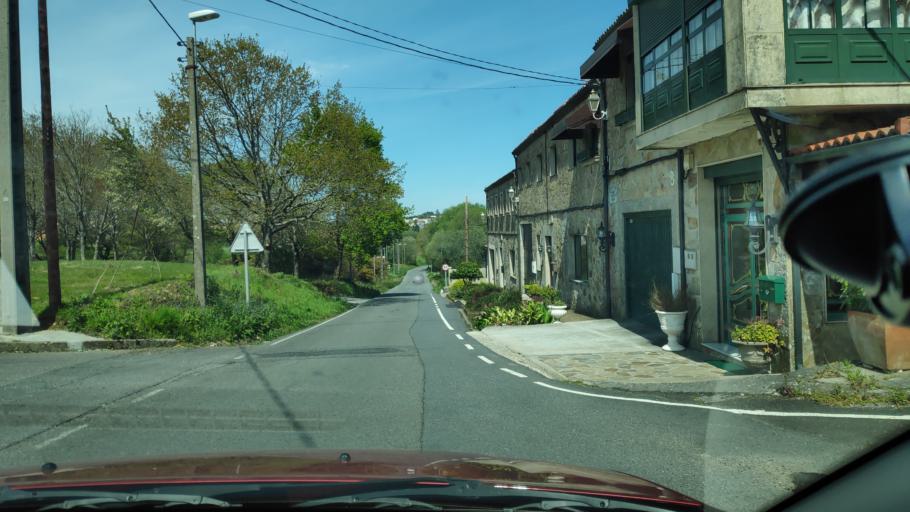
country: ES
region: Galicia
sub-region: Provincia da Coruna
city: Santiago de Compostela
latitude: 42.8920
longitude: -8.5259
